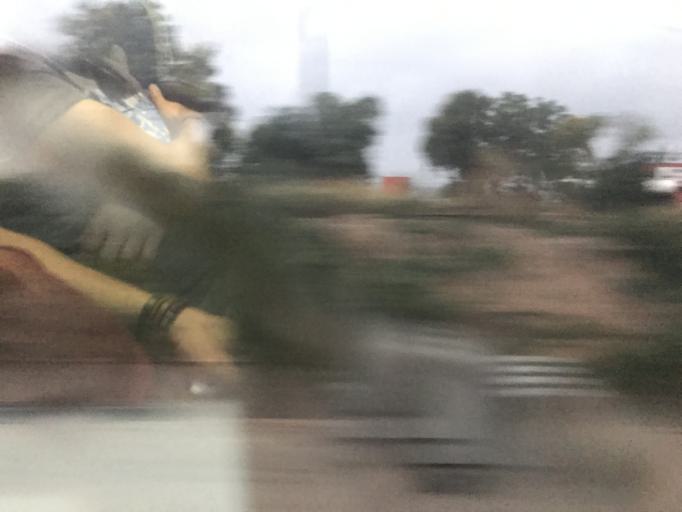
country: TR
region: Kocaeli
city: Hereke
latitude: 40.7829
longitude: 29.6115
